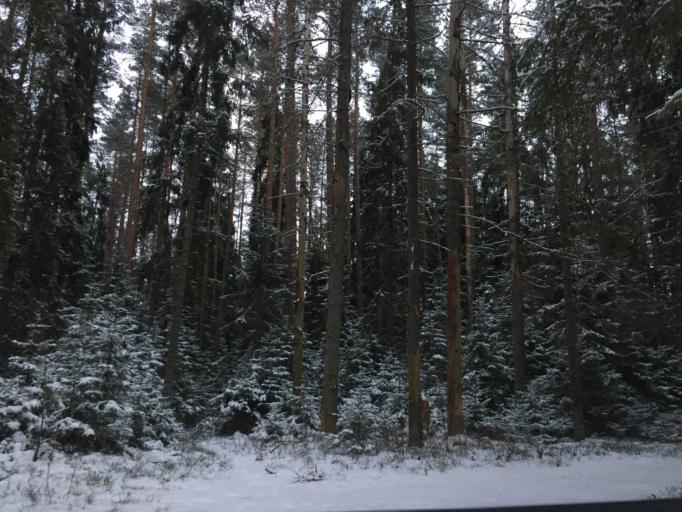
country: LV
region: Ligatne
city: Ligatne
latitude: 57.2390
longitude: 25.0532
